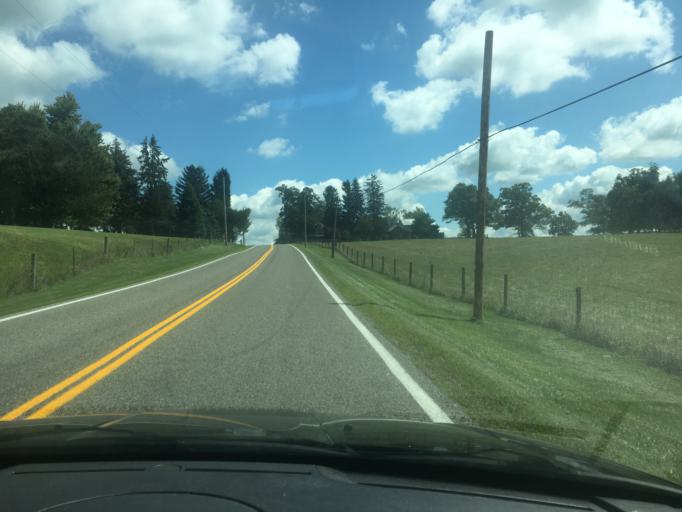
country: US
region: Ohio
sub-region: Logan County
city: West Liberty
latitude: 40.2340
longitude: -83.7213
